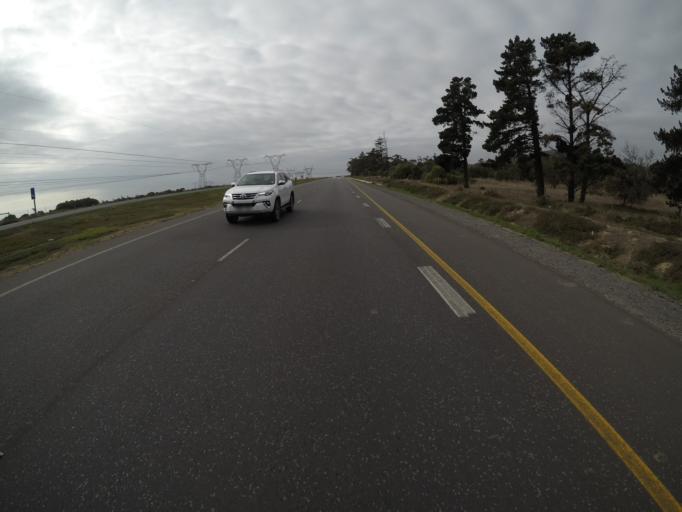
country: ZA
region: Western Cape
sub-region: City of Cape Town
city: Sunset Beach
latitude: -33.7302
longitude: 18.5450
